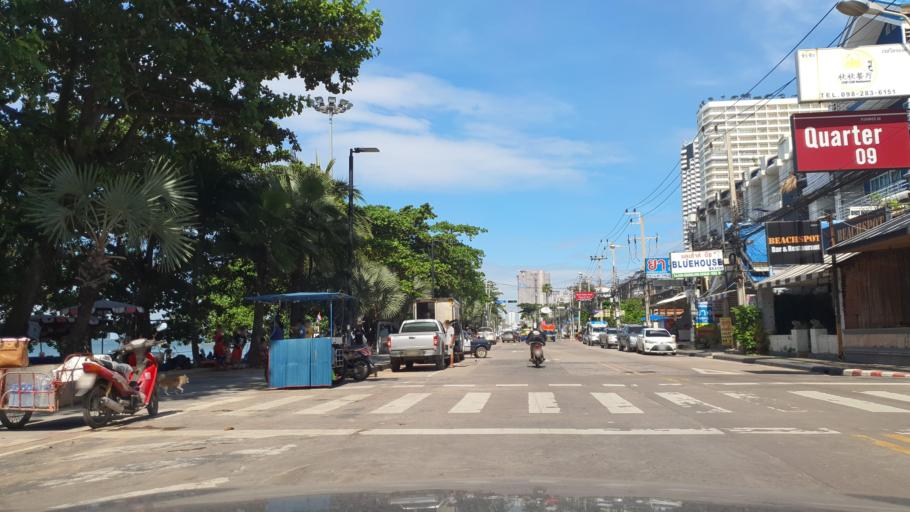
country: TH
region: Chon Buri
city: Phatthaya
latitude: 12.8763
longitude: 100.8859
